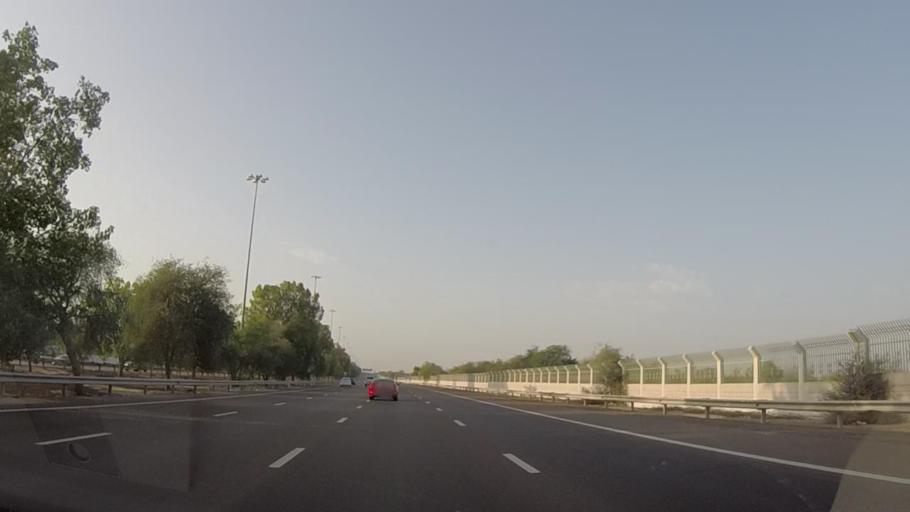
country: AE
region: Dubai
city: Dubai
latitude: 24.8130
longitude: 54.8704
